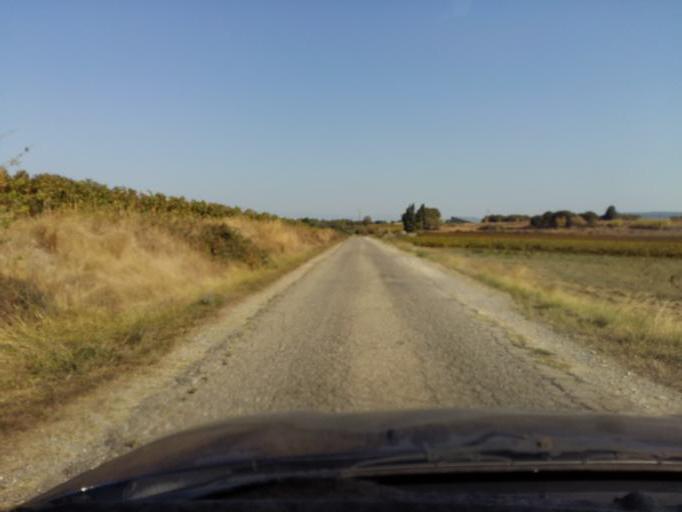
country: FR
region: Provence-Alpes-Cote d'Azur
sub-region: Departement du Vaucluse
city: Sainte-Cecile-les-Vignes
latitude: 44.2259
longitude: 4.8723
